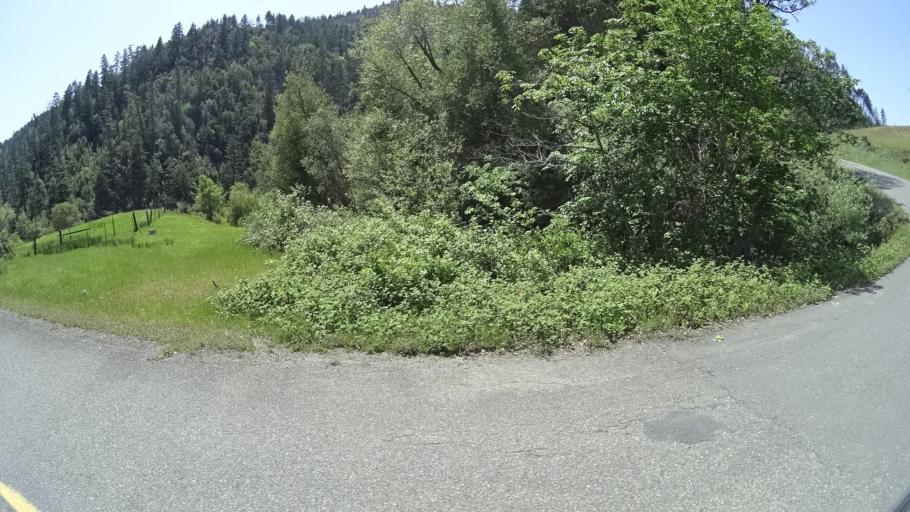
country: US
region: California
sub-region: Humboldt County
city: Redway
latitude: 40.2264
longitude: -123.6080
